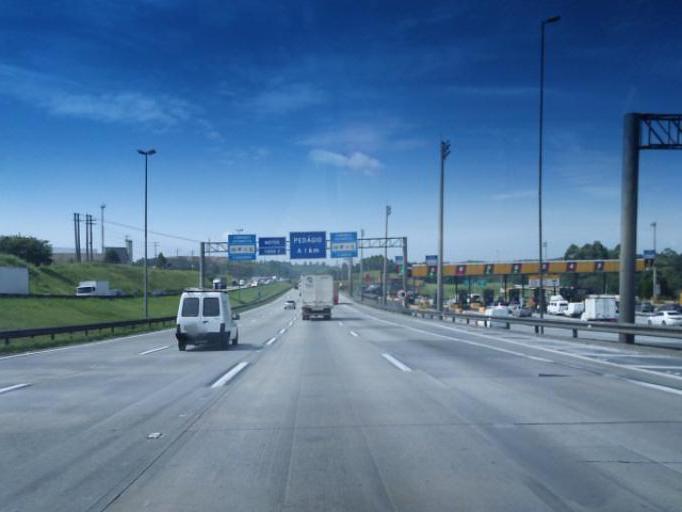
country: BR
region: Sao Paulo
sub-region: Taboao Da Serra
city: Taboao da Serra
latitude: -23.5880
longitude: -46.8093
